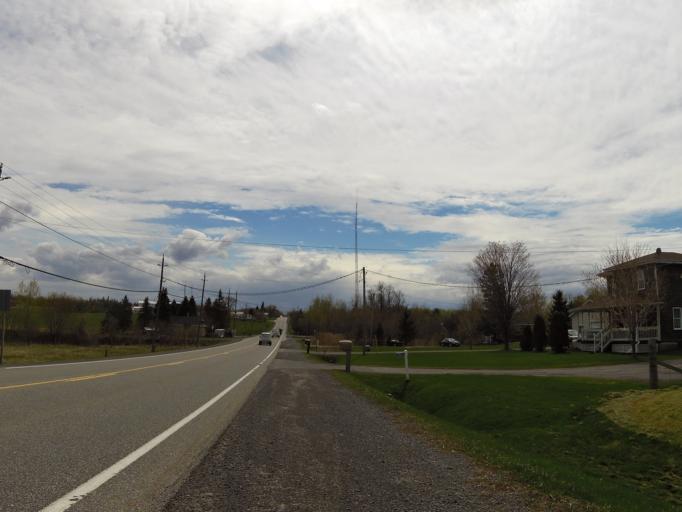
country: CA
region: Ontario
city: Hawkesbury
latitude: 45.5359
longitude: -74.6437
